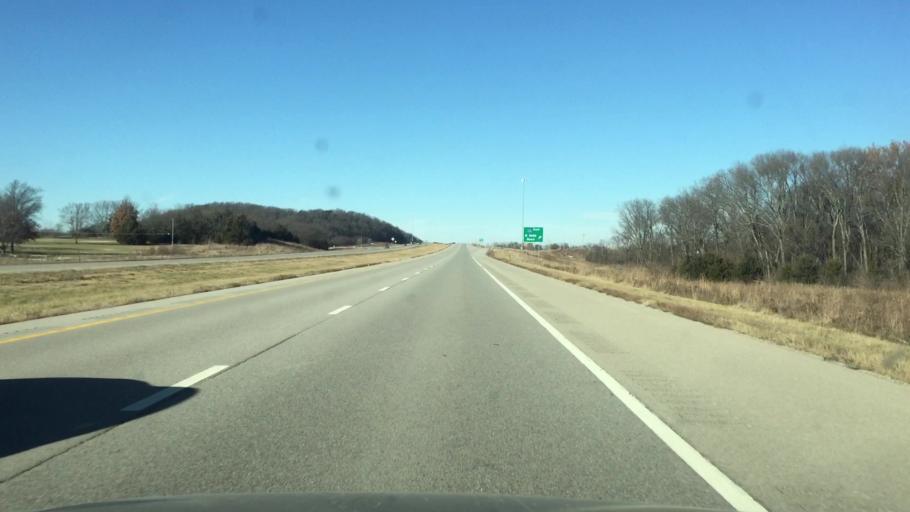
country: US
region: Kansas
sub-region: Douglas County
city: Lawrence
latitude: 38.8787
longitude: -95.2566
